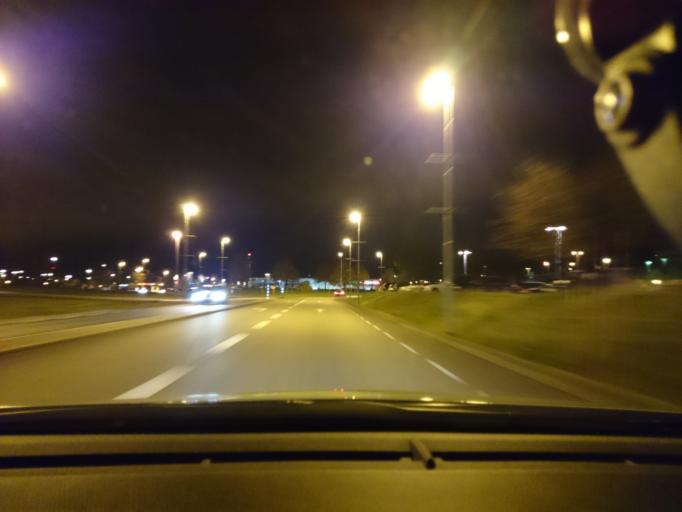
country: SE
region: Vaestra Goetaland
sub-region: Harryda Kommun
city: Landvetter
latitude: 57.6710
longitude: 12.3003
